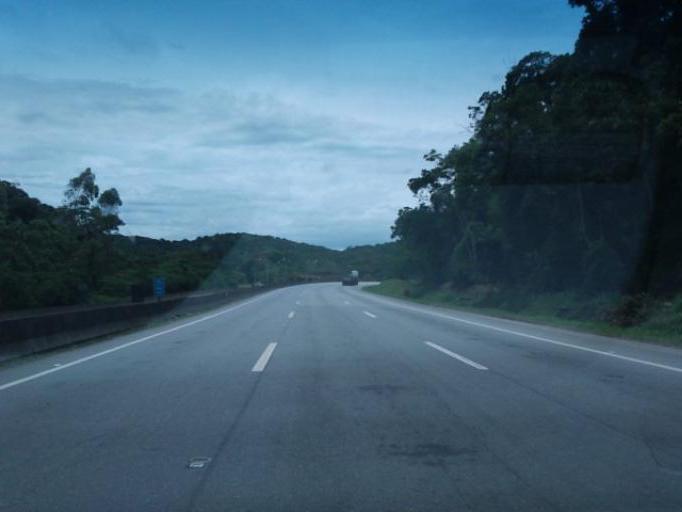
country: BR
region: Sao Paulo
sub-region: Juquitiba
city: Juquitiba
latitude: -24.0245
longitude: -47.1729
